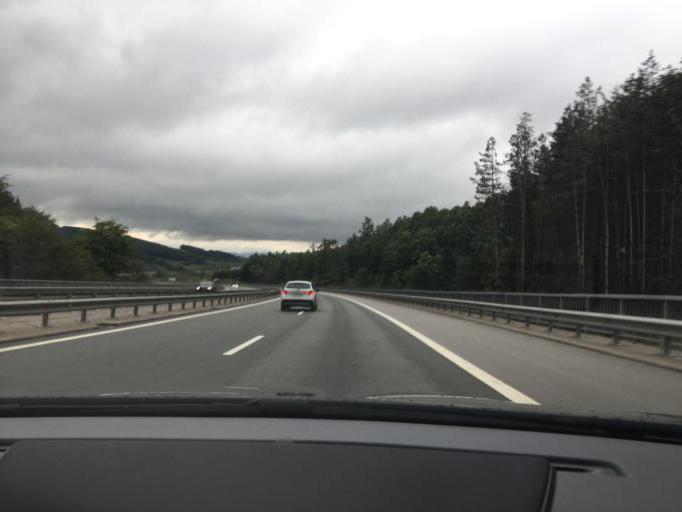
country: BG
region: Pernik
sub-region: Obshtina Pernik
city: Pernik
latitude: 42.6553
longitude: 23.1305
